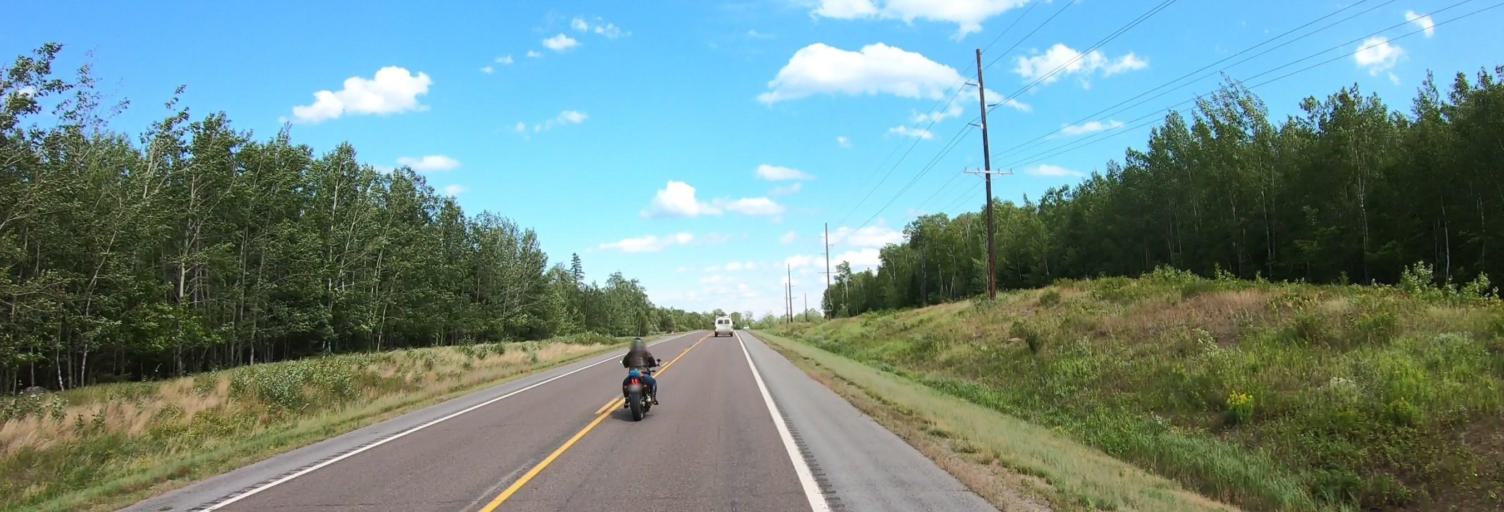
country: US
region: Minnesota
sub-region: Saint Louis County
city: Virginia
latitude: 47.8587
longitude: -92.4393
